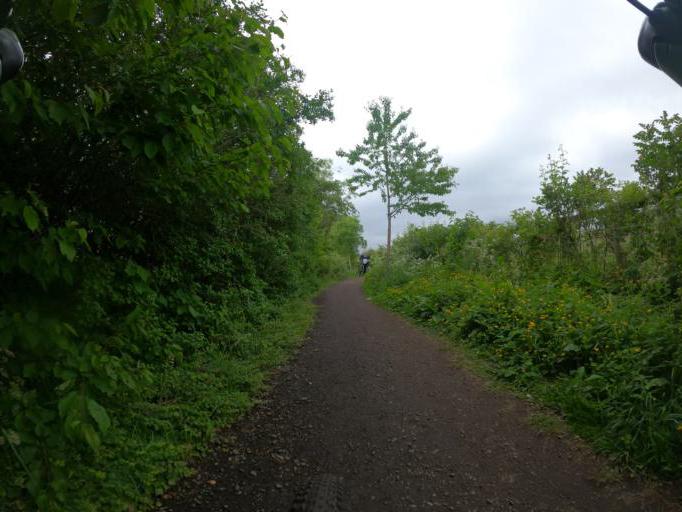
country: GB
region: Scotland
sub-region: Edinburgh
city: Currie
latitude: 55.9004
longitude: -3.2871
